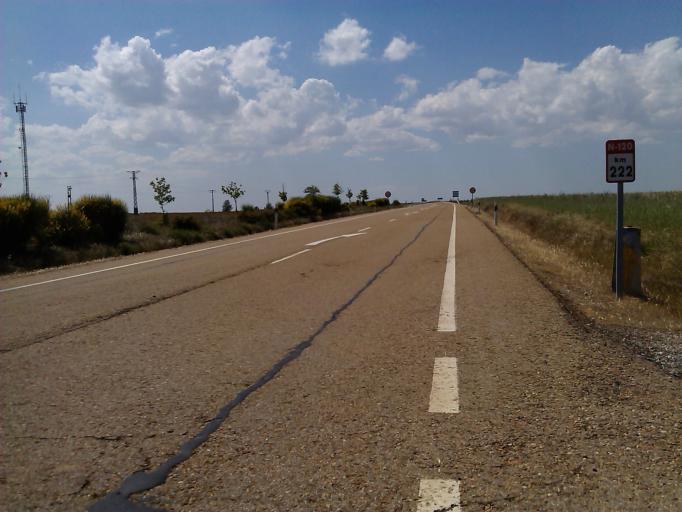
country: ES
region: Castille and Leon
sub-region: Provincia de Palencia
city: Ledigos
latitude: 42.3475
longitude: -4.8547
